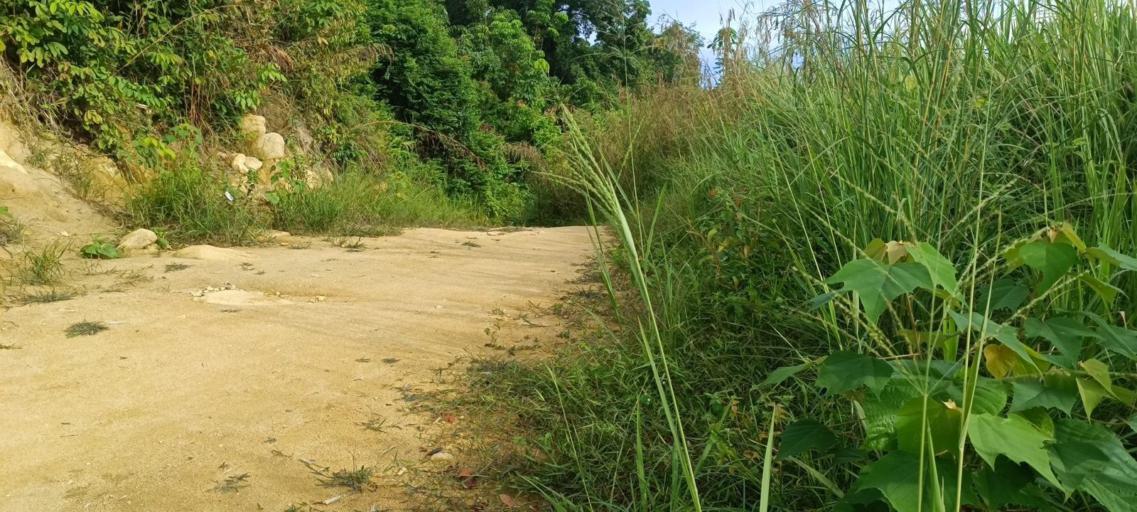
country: MY
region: Penang
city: Nibong Tebal
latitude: 5.2302
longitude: 100.5141
